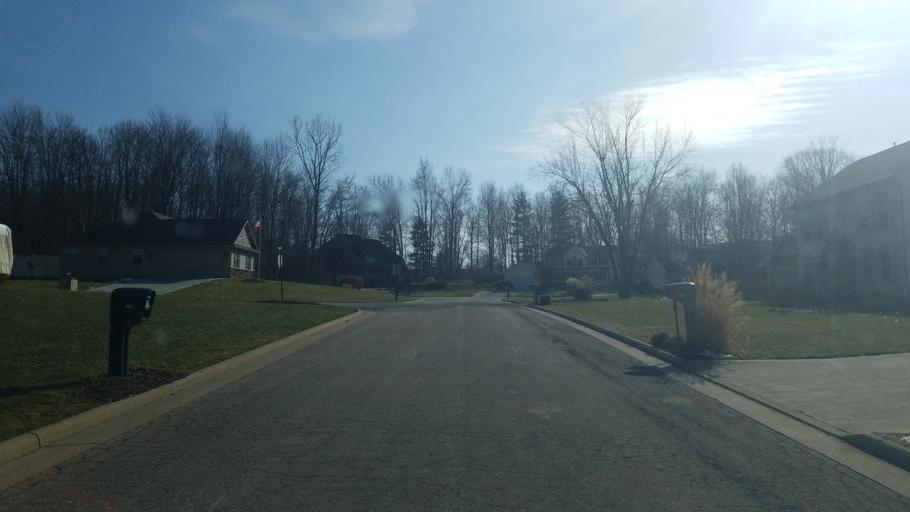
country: US
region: Ohio
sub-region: Richland County
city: Ontario
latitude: 40.7776
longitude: -82.6443
